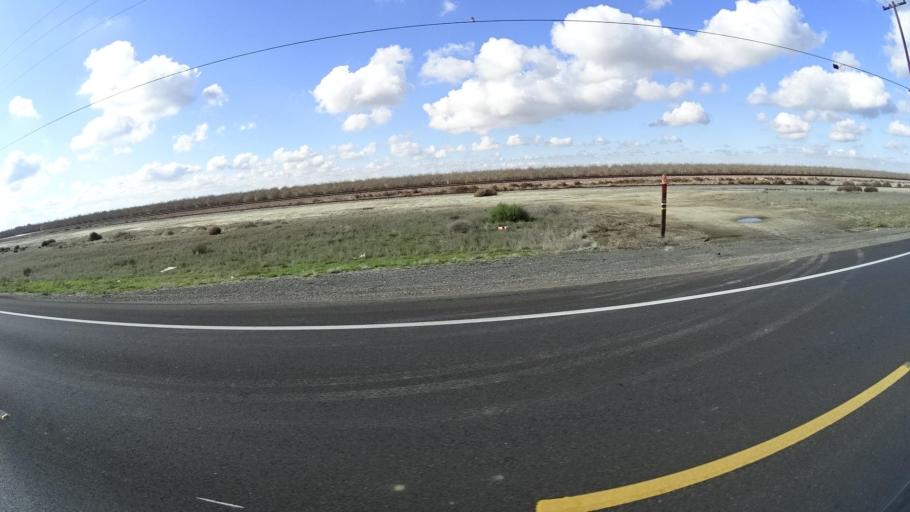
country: US
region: California
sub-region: Kern County
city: Wasco
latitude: 35.6775
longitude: -119.3300
